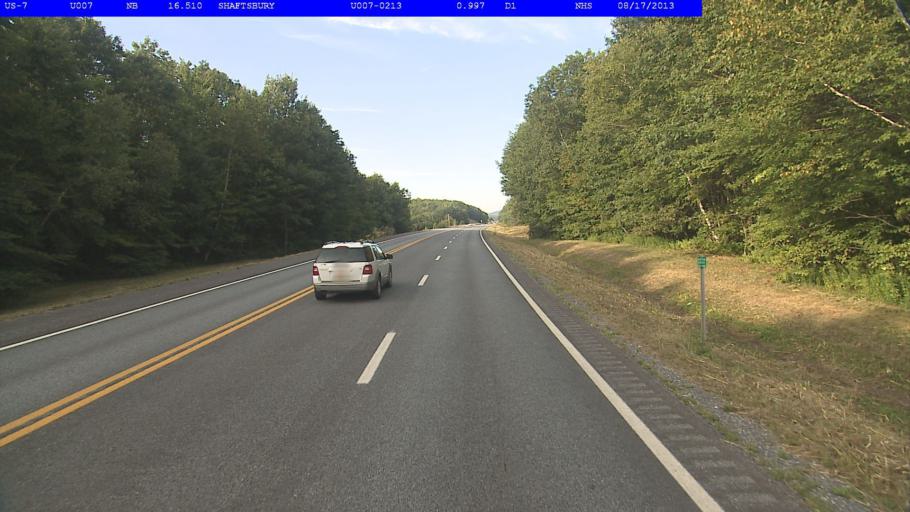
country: US
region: Vermont
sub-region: Bennington County
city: North Bennington
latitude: 42.9449
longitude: -73.1792
